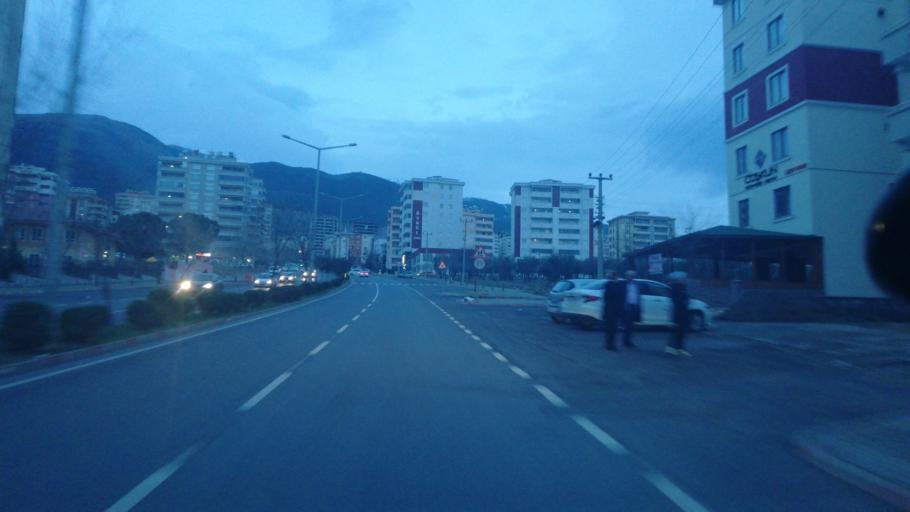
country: TR
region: Kahramanmaras
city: Kahramanmaras
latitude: 37.5874
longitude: 36.8620
